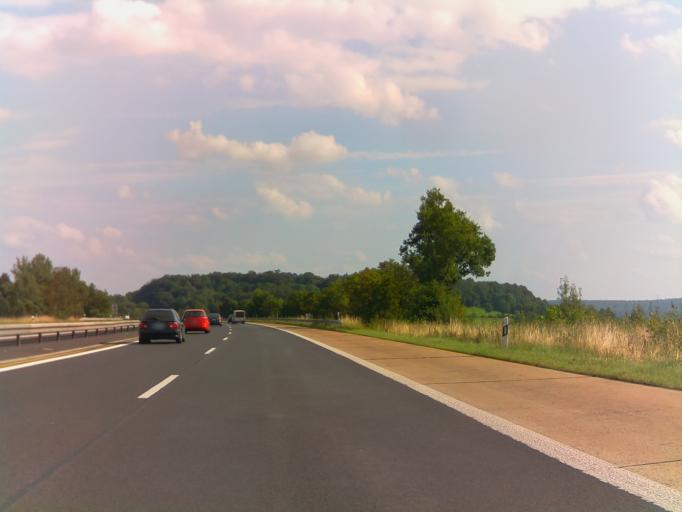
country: DE
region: Bavaria
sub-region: Regierungsbezirk Unterfranken
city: Schondra
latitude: 50.2878
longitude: 9.8540
